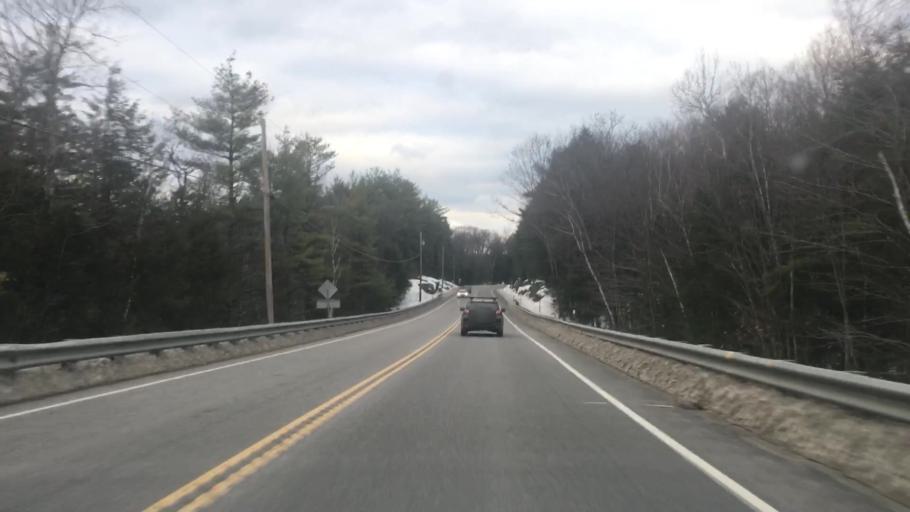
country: US
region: New Hampshire
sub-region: Hillsborough County
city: Antrim
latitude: 43.0778
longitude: -71.9919
